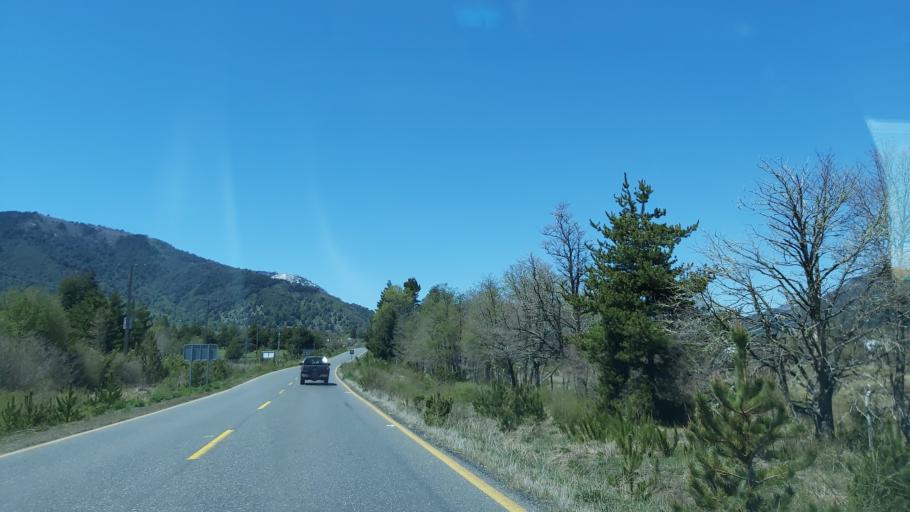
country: CL
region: Araucania
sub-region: Provincia de Cautin
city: Vilcun
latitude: -38.4636
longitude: -71.6195
